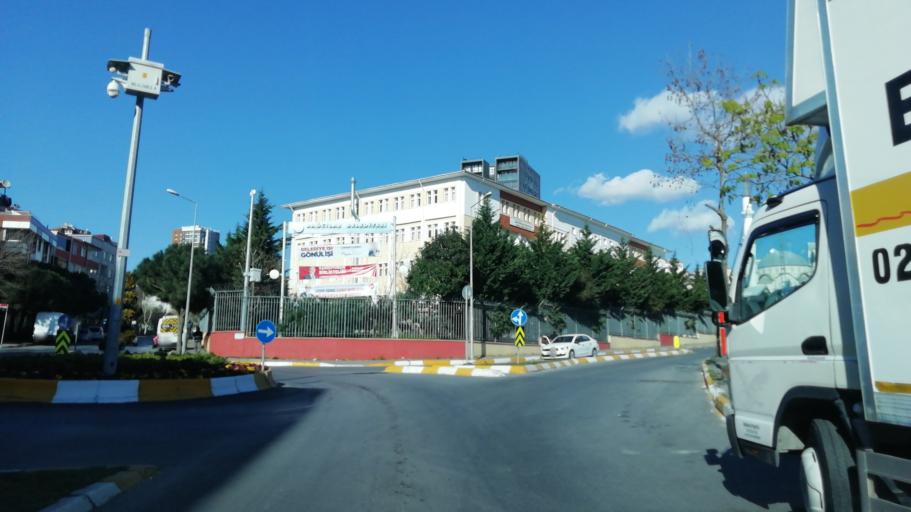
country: TR
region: Istanbul
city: Bagcilar
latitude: 41.0478
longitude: 28.8546
